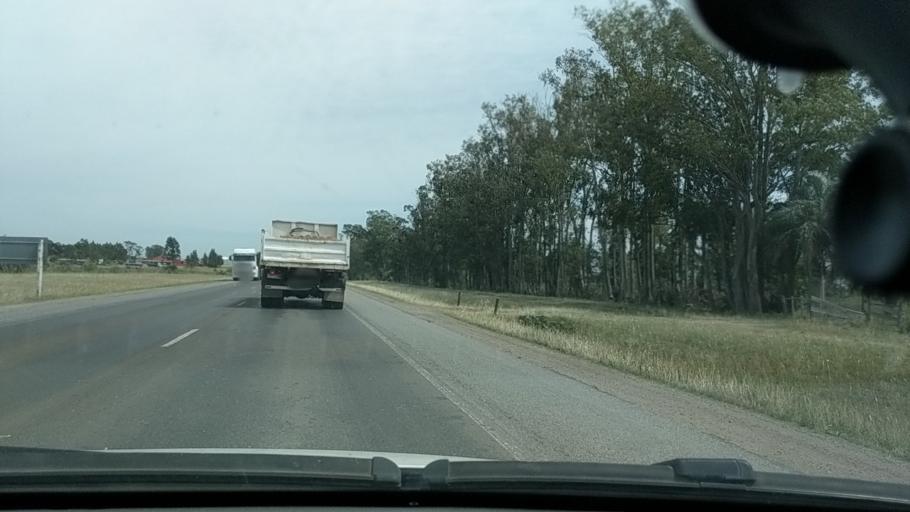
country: UY
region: Durazno
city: Durazno
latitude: -33.4273
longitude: -56.4977
